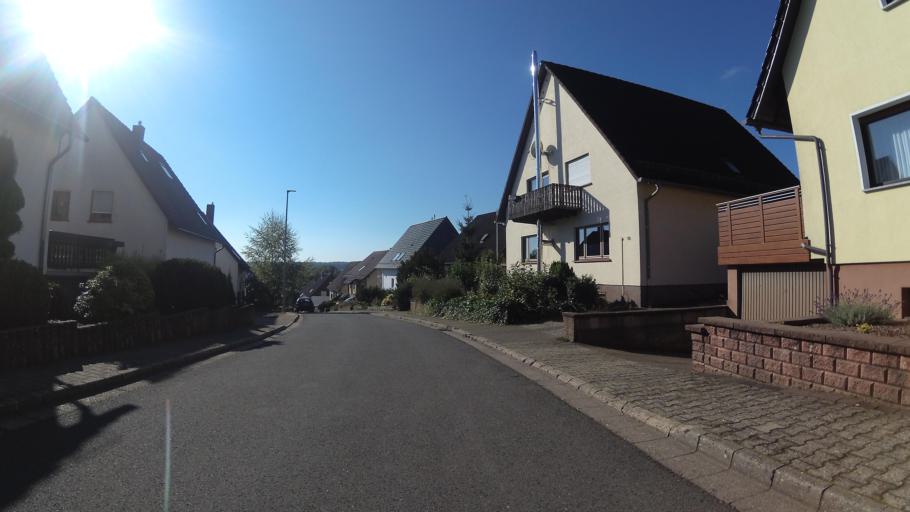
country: DE
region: Rheinland-Pfalz
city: Waldmohr
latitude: 49.3936
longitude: 7.3309
